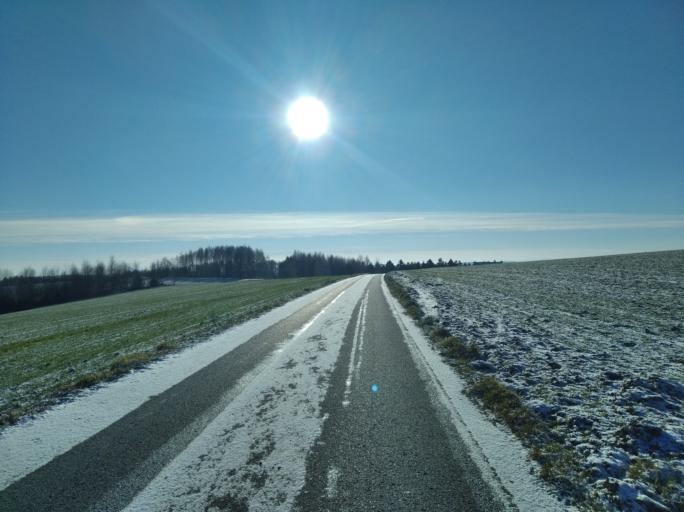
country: PL
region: Subcarpathian Voivodeship
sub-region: Powiat ropczycko-sedziszowski
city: Iwierzyce
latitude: 49.9678
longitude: 21.7497
